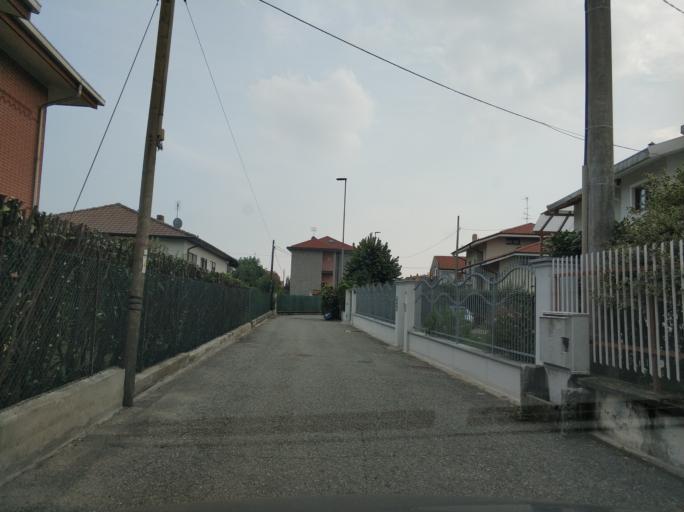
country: IT
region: Piedmont
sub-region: Provincia di Torino
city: Caselle Torinese
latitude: 45.1827
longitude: 7.6437
